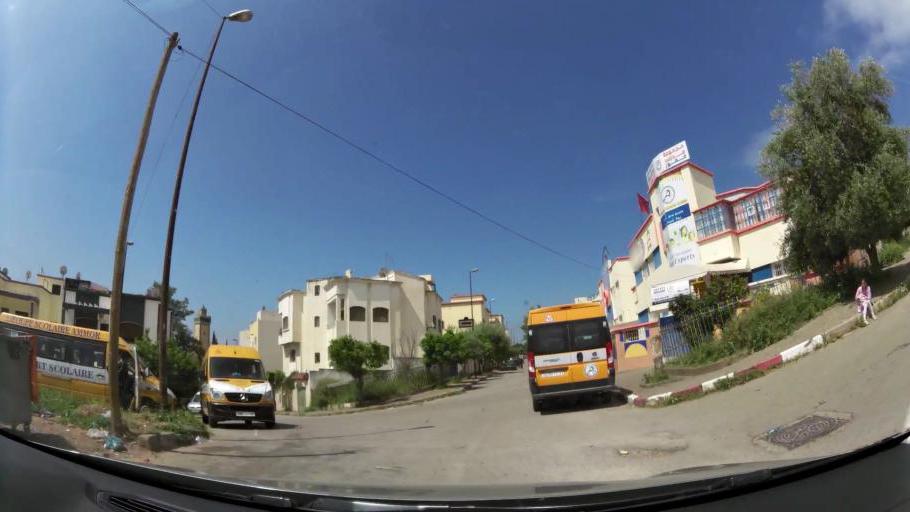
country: MA
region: Fes-Boulemane
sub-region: Fes
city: Fes
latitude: 34.0616
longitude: -5.0355
